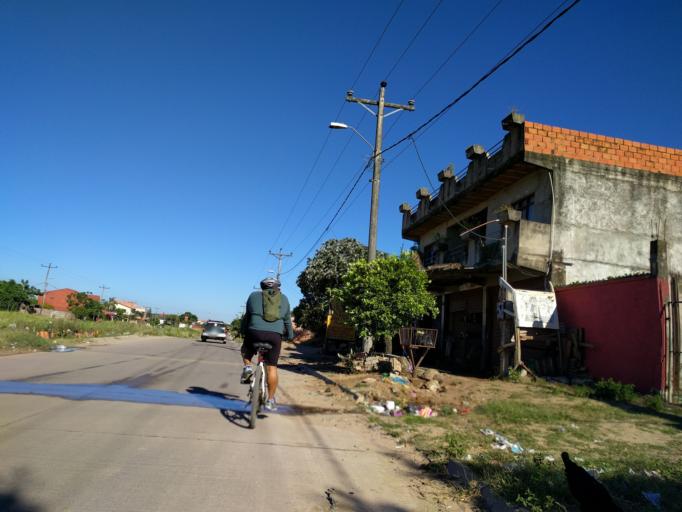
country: BO
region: Santa Cruz
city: Santa Cruz de la Sierra
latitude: -17.8484
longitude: -63.2429
